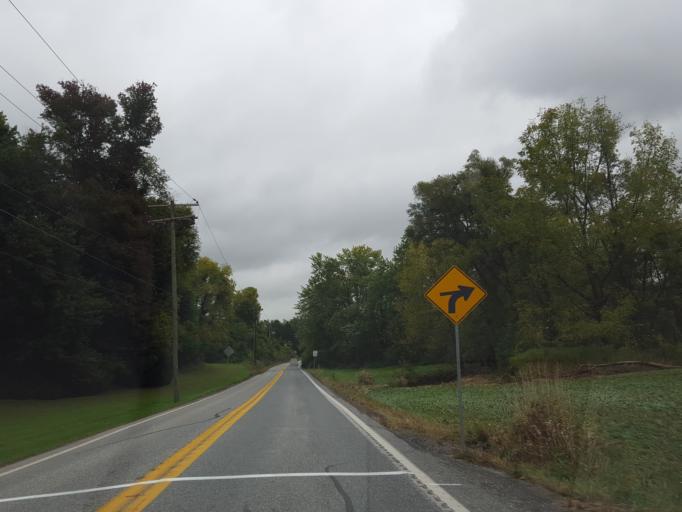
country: US
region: Pennsylvania
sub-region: York County
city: Spry
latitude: 39.9432
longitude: -76.6566
